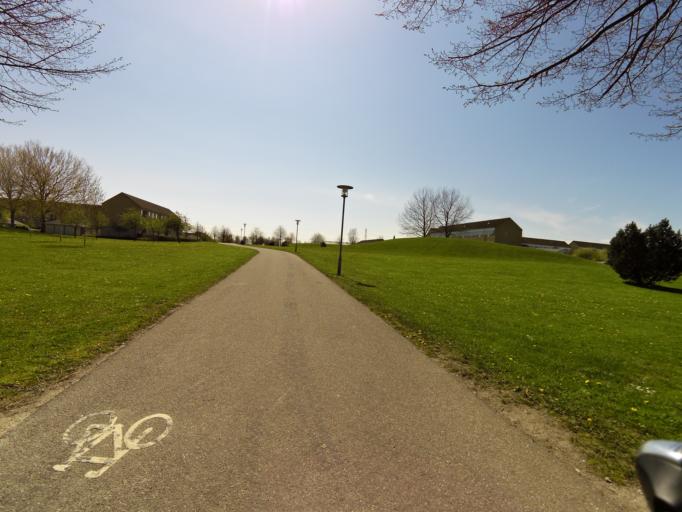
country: DK
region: Capital Region
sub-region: Hoje-Taastrup Kommune
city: Taastrup
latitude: 55.6377
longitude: 12.2729
